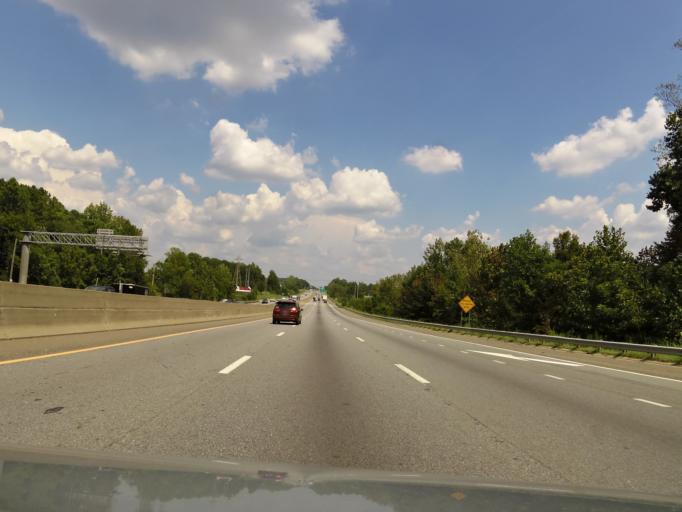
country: US
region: North Carolina
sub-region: Gaston County
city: Bessemer City
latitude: 35.2676
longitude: -81.2537
